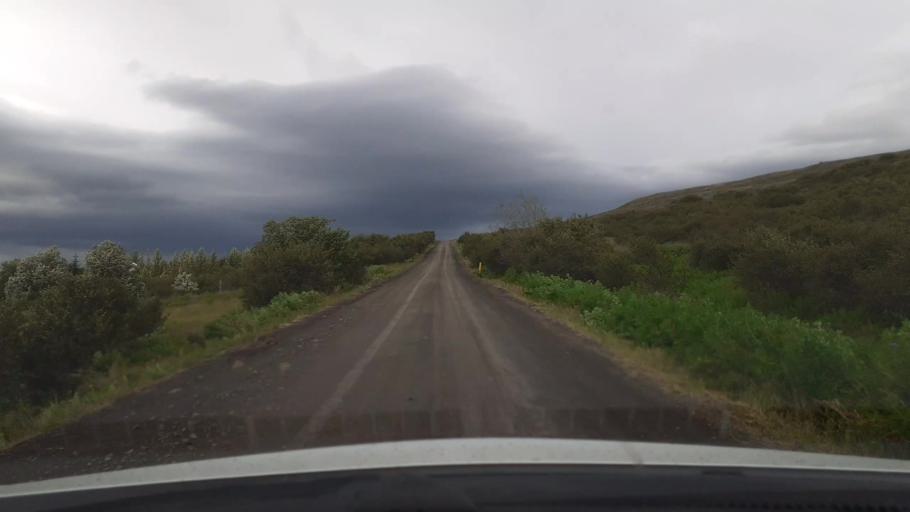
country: IS
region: Capital Region
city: Mosfellsbaer
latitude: 64.5235
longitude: -21.4722
